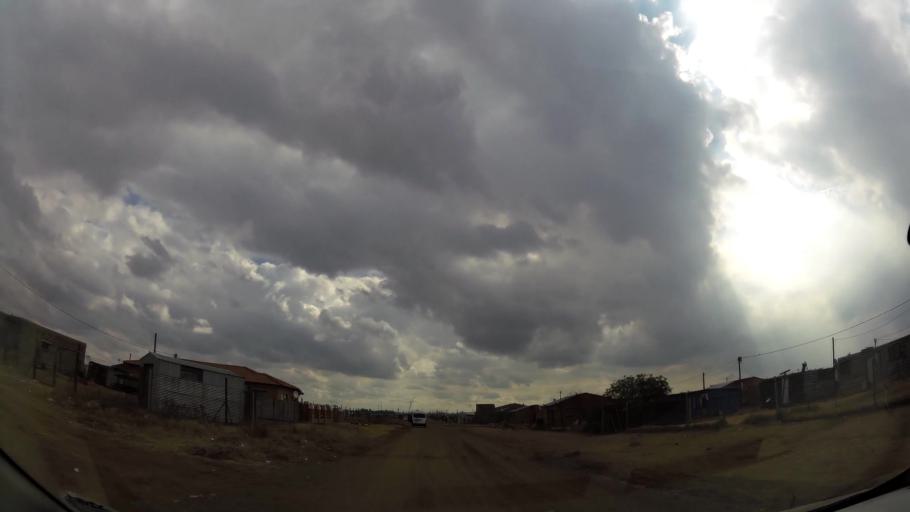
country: ZA
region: Orange Free State
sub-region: Fezile Dabi District Municipality
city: Sasolburg
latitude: -26.8530
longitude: 27.8947
